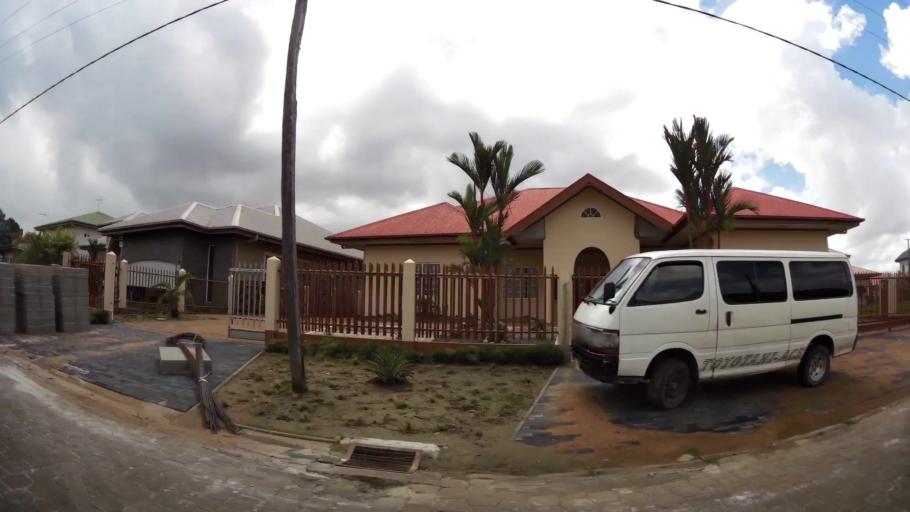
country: SR
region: Paramaribo
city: Paramaribo
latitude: 5.8372
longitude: -55.1943
